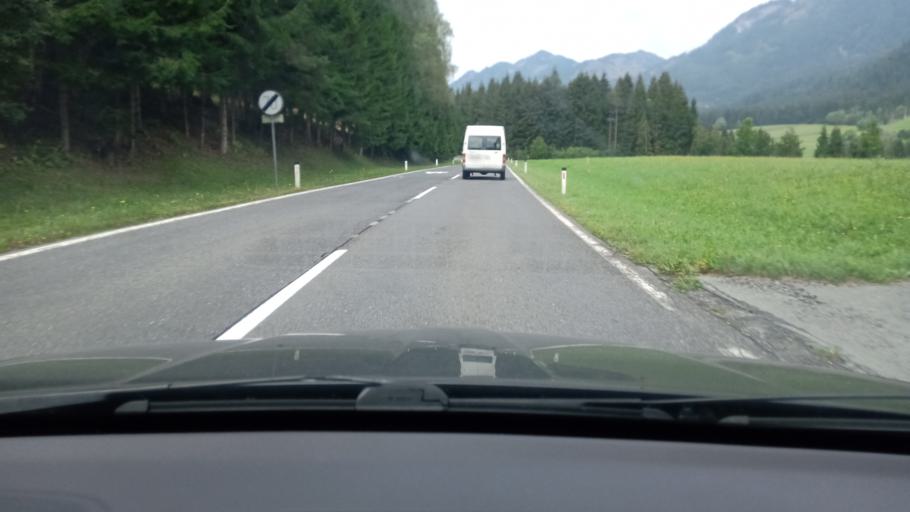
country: AT
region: Carinthia
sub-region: Politischer Bezirk Hermagor
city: Hermagor
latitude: 46.6466
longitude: 13.3342
